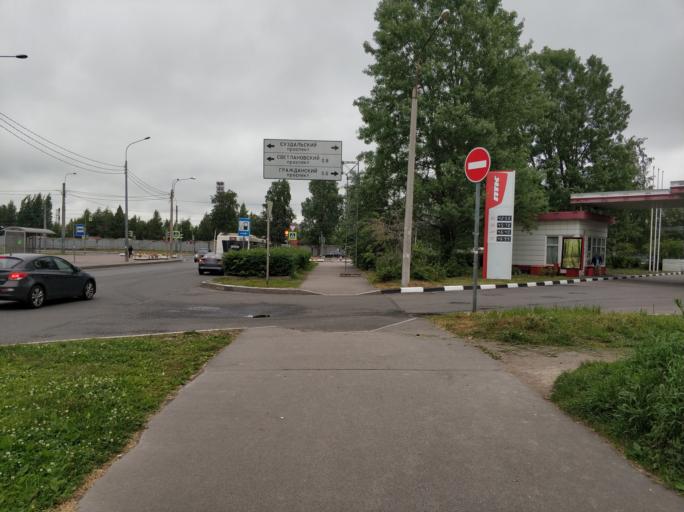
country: RU
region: St.-Petersburg
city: Grazhdanka
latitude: 60.0443
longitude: 30.4174
